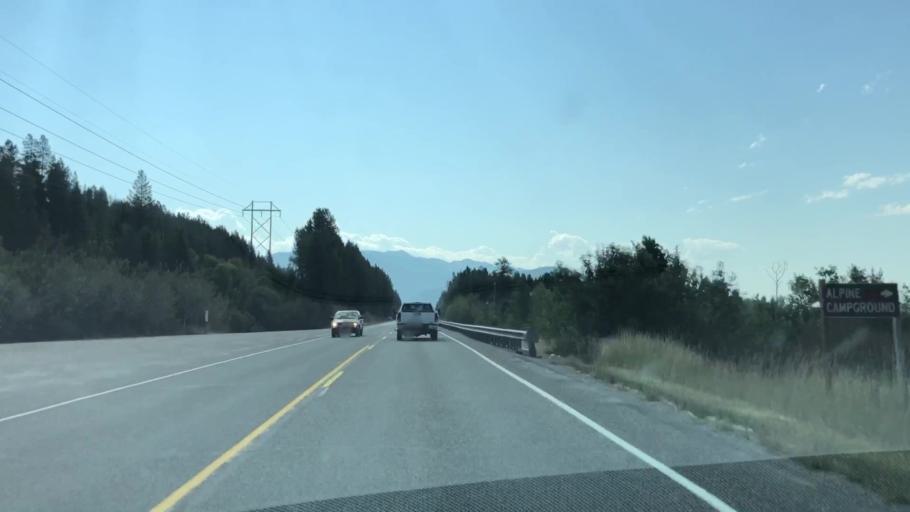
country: US
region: Wyoming
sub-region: Teton County
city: Hoback
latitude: 43.2017
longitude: -111.0449
